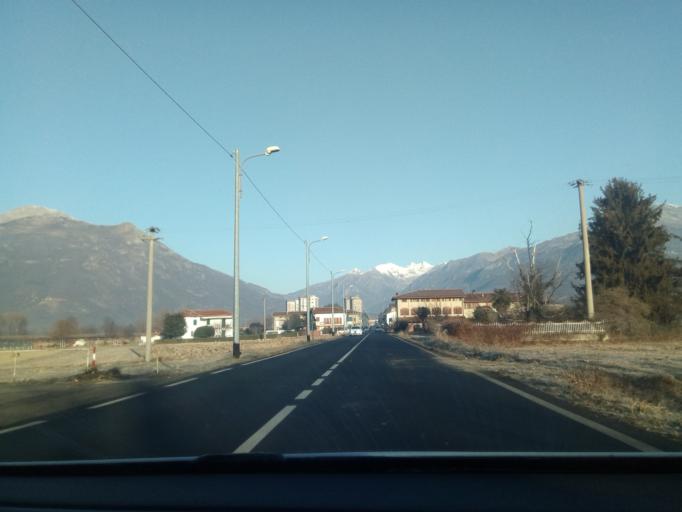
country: IT
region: Piedmont
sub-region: Provincia di Torino
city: Montalto Dora
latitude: 45.4770
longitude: 7.8661
